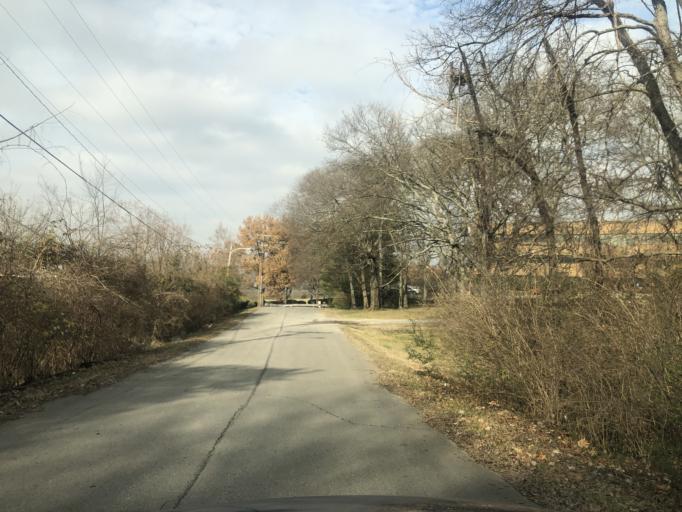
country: US
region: Tennessee
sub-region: Davidson County
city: Oak Hill
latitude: 36.0833
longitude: -86.6965
